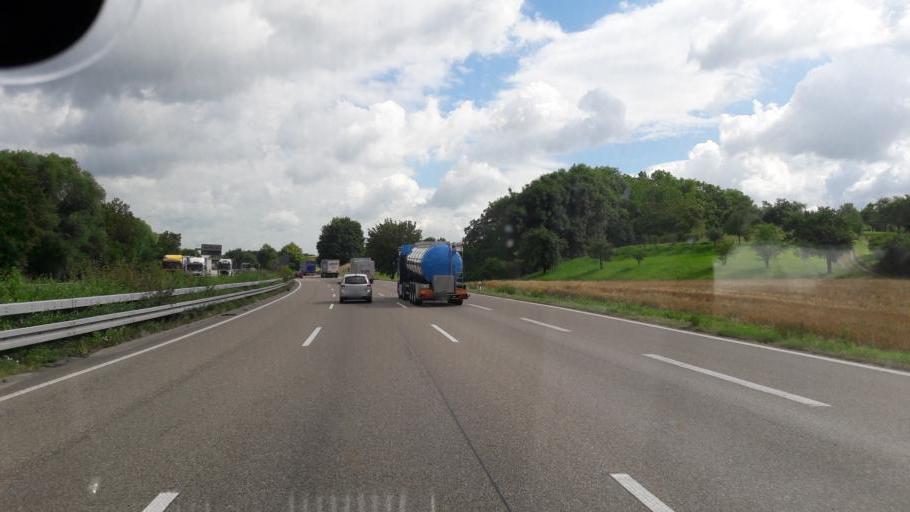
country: DE
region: Baden-Wuerttemberg
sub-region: Regierungsbezirk Stuttgart
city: Bretzfeld
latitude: 49.1815
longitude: 9.4142
